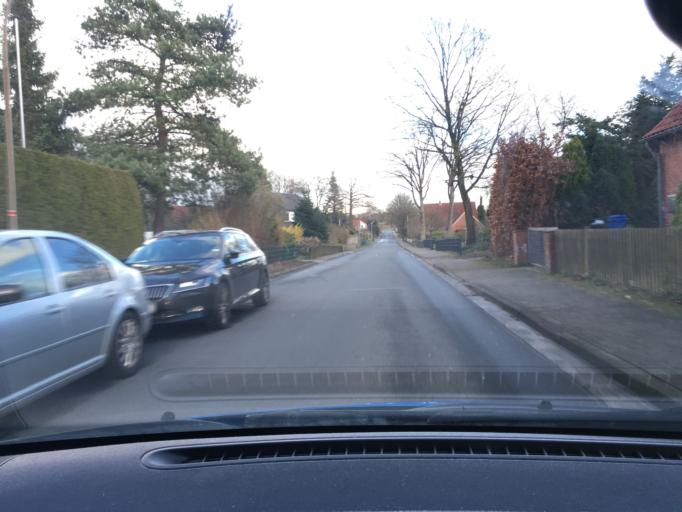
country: DE
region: Lower Saxony
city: Marxen
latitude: 53.3105
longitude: 9.9981
